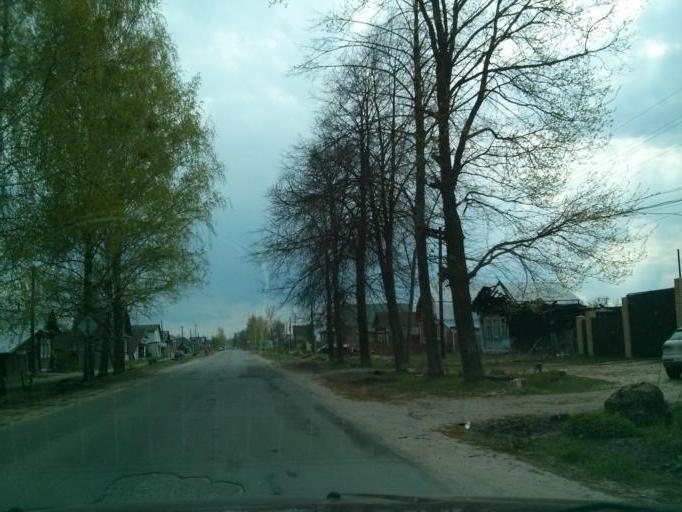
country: RU
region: Nizjnij Novgorod
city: Shimorskoye
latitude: 55.3402
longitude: 41.9288
